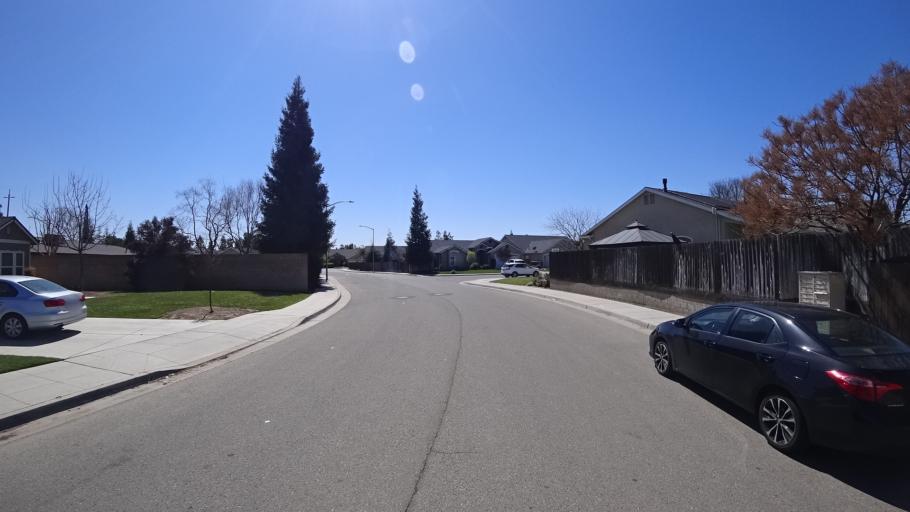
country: US
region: California
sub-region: Fresno County
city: West Park
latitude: 36.7751
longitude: -119.8811
